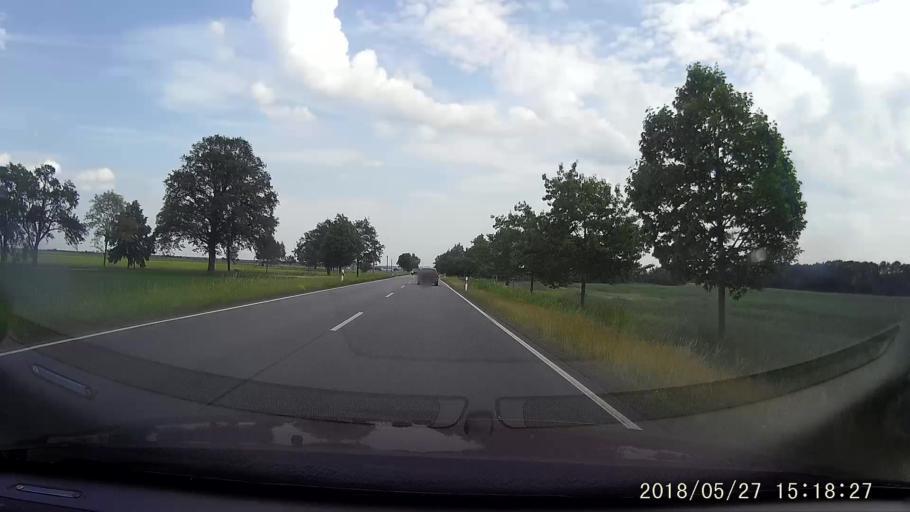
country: DE
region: Saxony
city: Kodersdorf
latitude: 51.2650
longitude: 14.8570
